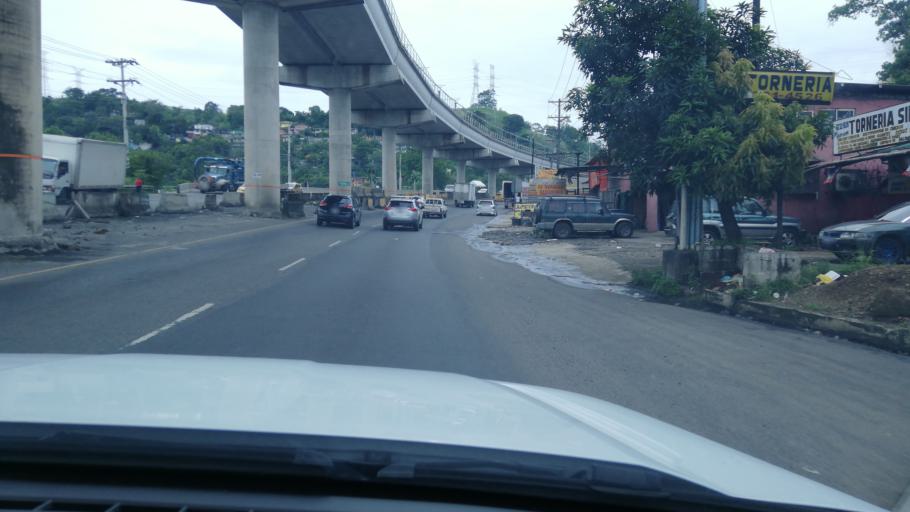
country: PA
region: Panama
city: Las Cumbres
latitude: 9.0638
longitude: -79.5116
